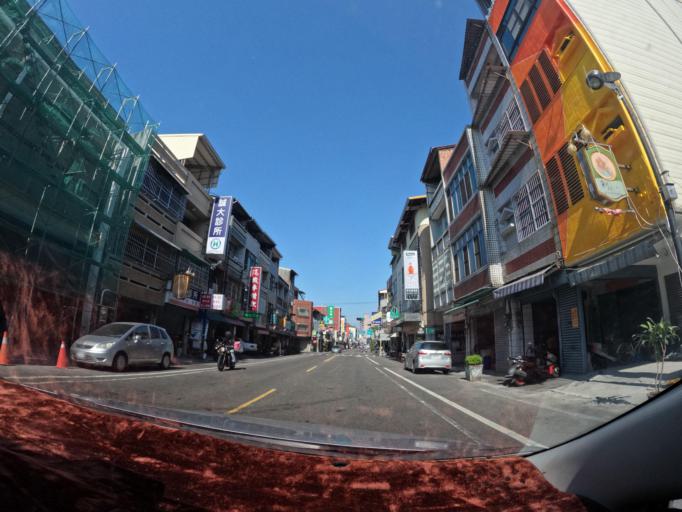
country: TW
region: Taiwan
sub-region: Tainan
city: Tainan
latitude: 23.0372
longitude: 120.3078
